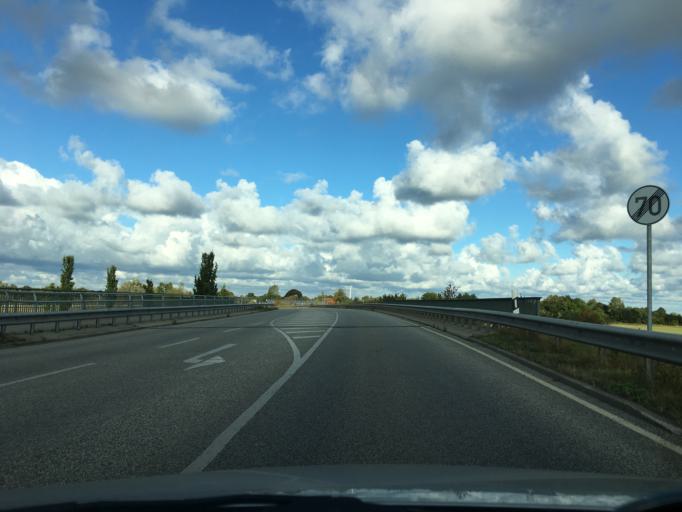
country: DE
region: Schleswig-Holstein
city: Brodersdorf
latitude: 54.3801
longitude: 10.2542
